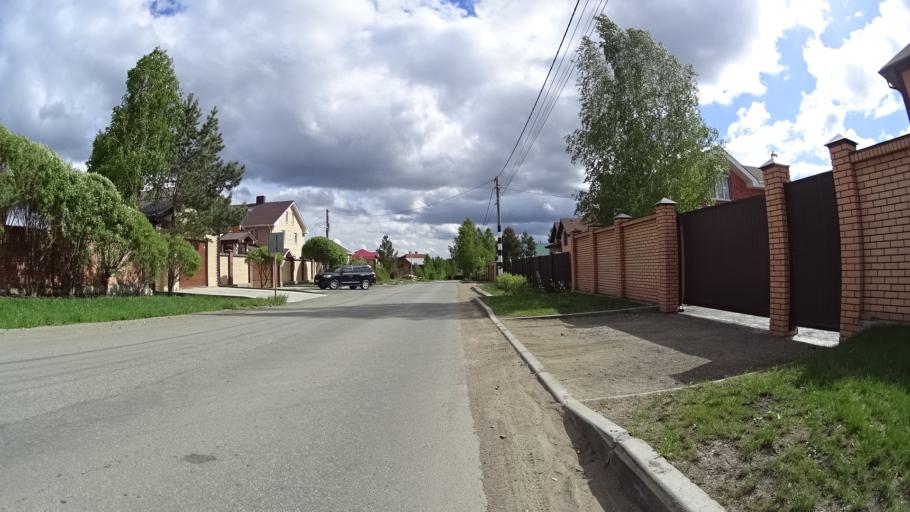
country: RU
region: Chelyabinsk
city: Sargazy
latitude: 55.1600
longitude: 61.2431
